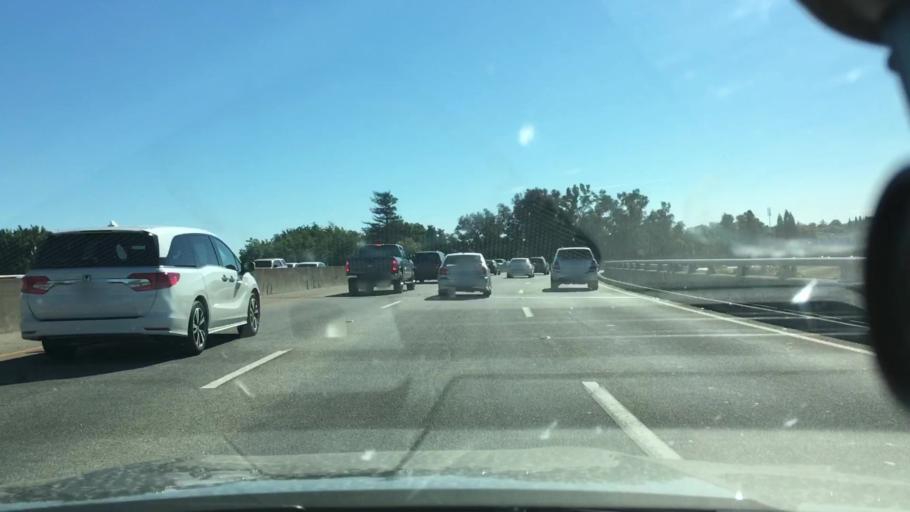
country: US
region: California
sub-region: Sacramento County
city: Sacramento
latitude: 38.5882
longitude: -121.4469
